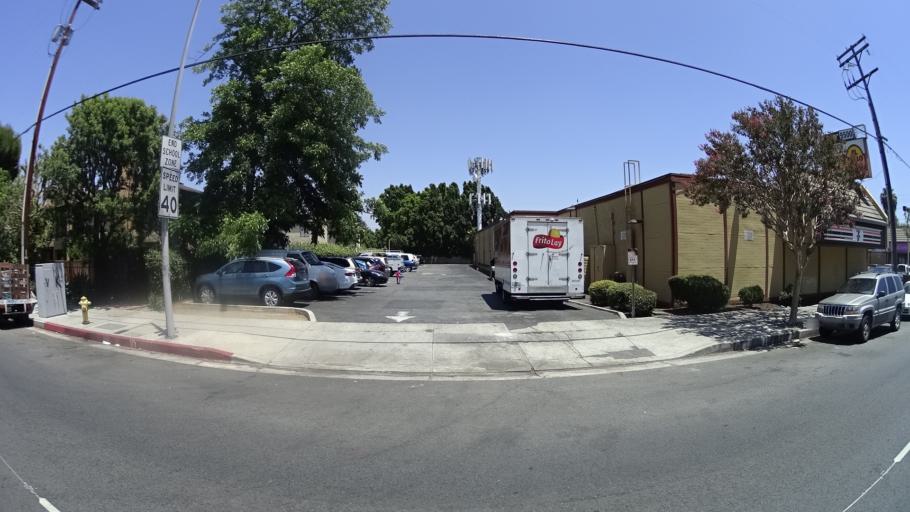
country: US
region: California
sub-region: Los Angeles County
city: San Fernando
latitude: 34.2434
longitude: -118.4674
